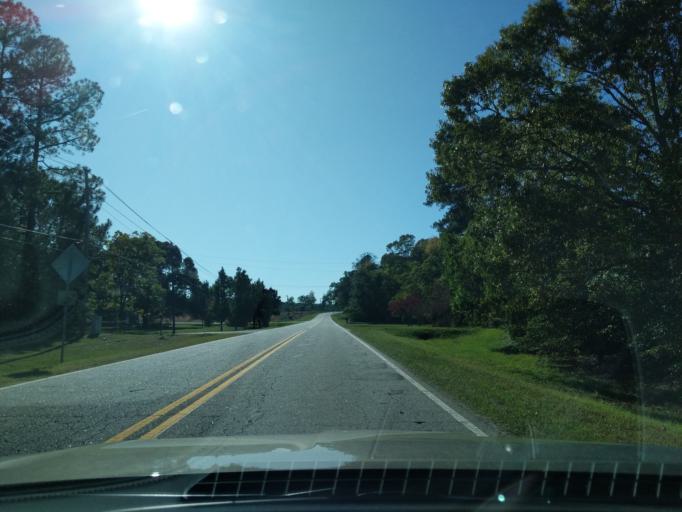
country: US
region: Georgia
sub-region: Columbia County
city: Grovetown
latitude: 33.4688
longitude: -82.1568
